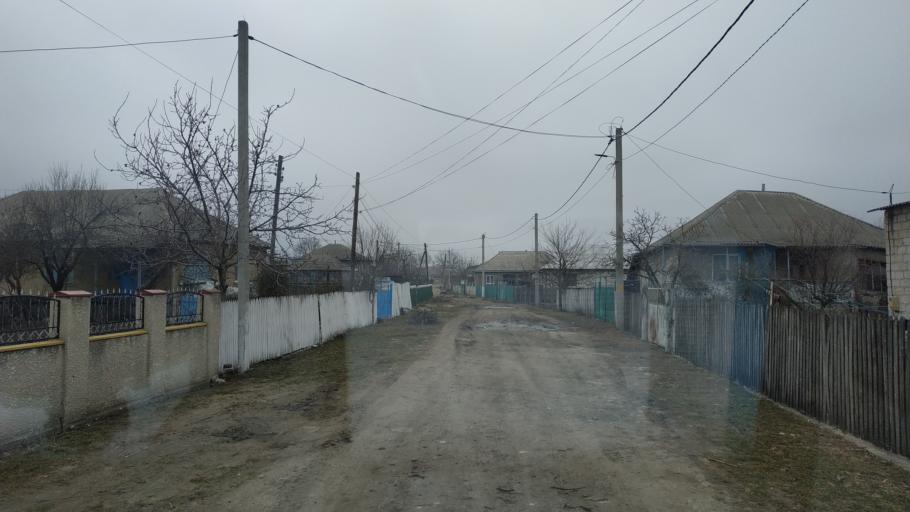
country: MD
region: Hincesti
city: Hincesti
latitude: 46.8917
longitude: 28.5471
